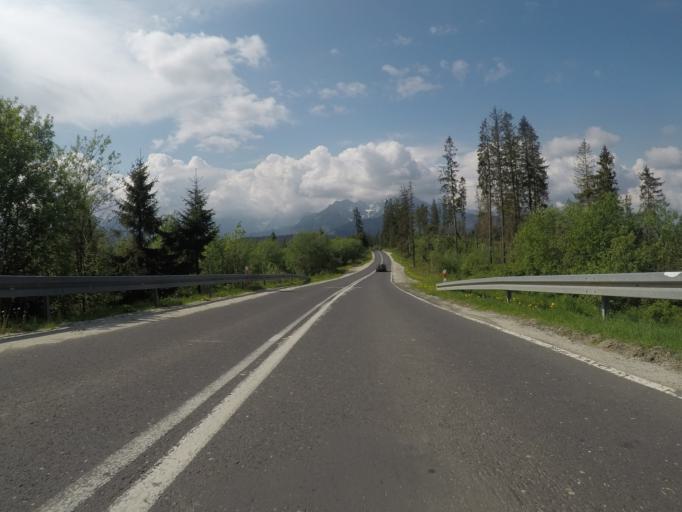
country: PL
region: Lesser Poland Voivodeship
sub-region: Powiat tatrzanski
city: Bukowina Tatrzanska
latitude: 49.2998
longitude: 20.1178
